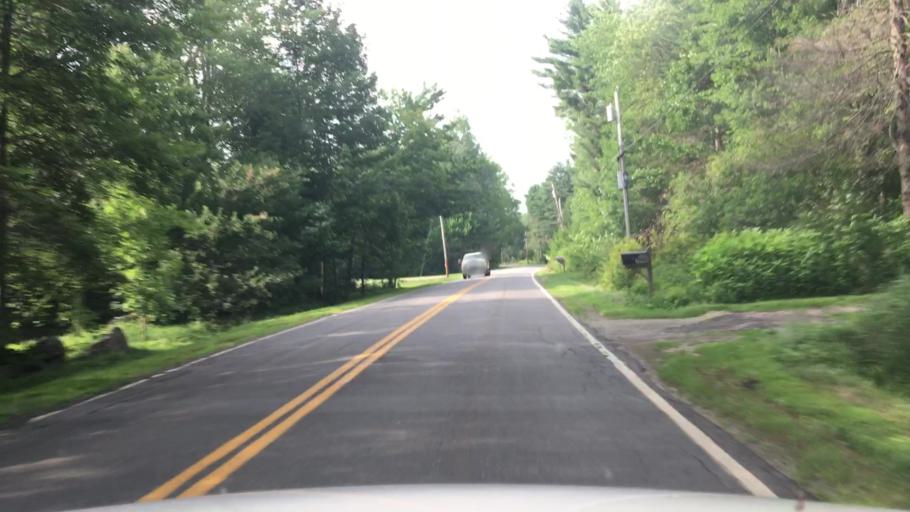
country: US
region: Maine
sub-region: Lincoln County
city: Waldoboro
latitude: 44.1624
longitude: -69.3778
